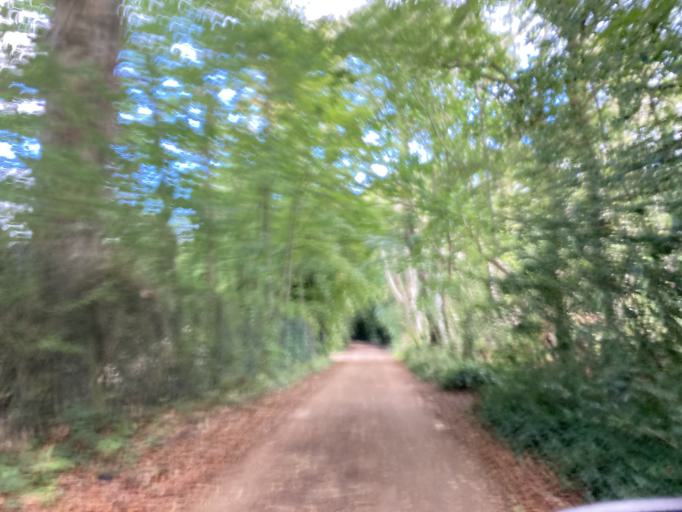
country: GB
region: England
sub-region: Isle of Wight
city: Shanklin
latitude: 50.6392
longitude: -1.1840
